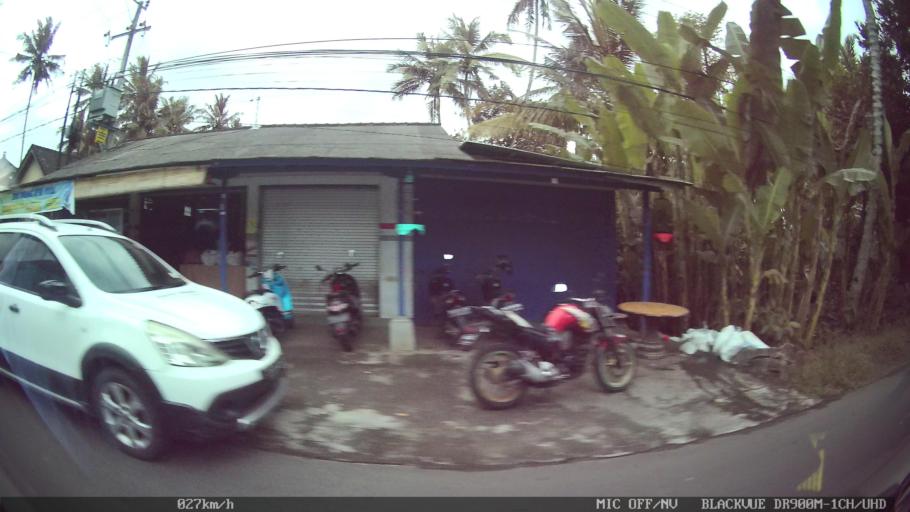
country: ID
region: Bali
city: Banjar Parekan
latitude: -8.5662
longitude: 115.2110
